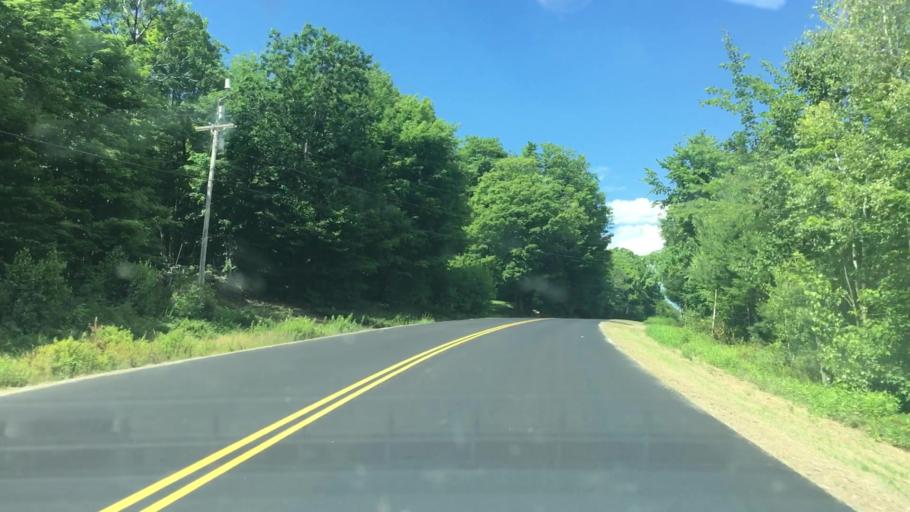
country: US
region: Maine
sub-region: Franklin County
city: Jay
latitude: 44.5478
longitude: -70.1888
